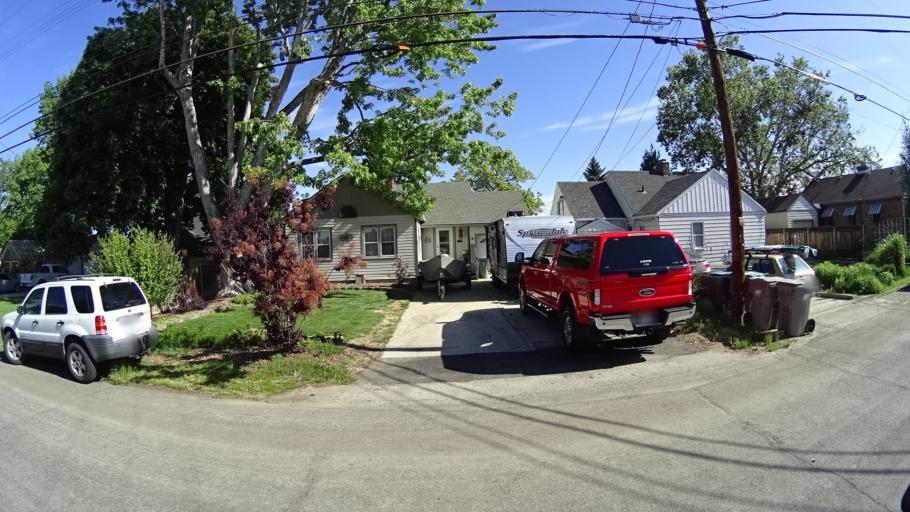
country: US
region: Idaho
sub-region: Ada County
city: Garden City
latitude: 43.6203
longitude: -116.2420
